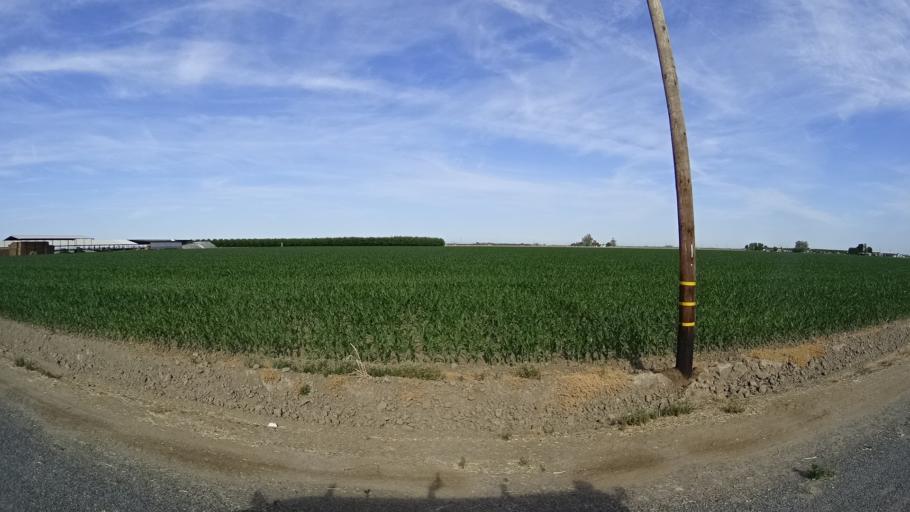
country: US
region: California
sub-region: Kings County
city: Hanford
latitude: 36.3677
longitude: -119.5470
